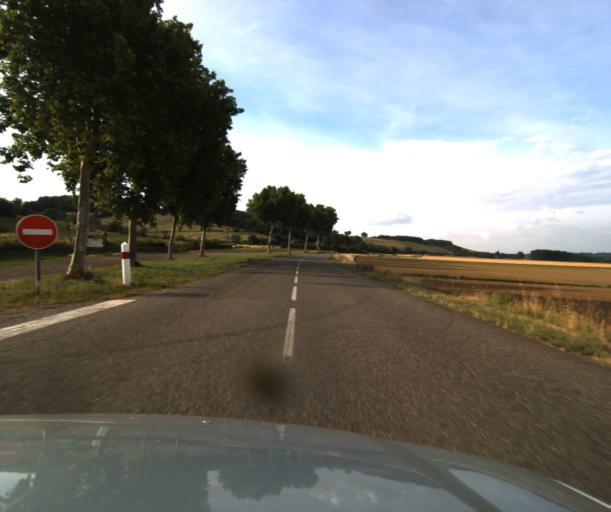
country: FR
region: Midi-Pyrenees
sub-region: Departement du Tarn-et-Garonne
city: Castelsarrasin
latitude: 43.9569
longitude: 1.1030
